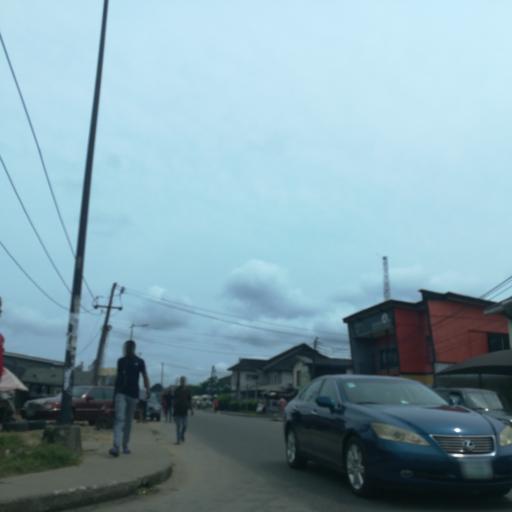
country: NG
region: Rivers
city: Port Harcourt
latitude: 4.8034
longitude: 7.0064
